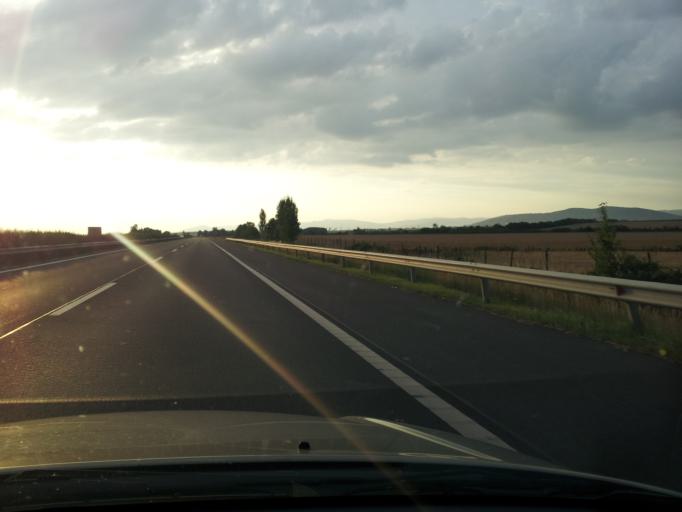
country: HU
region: Heves
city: Adacs
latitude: 47.7192
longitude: 19.9940
